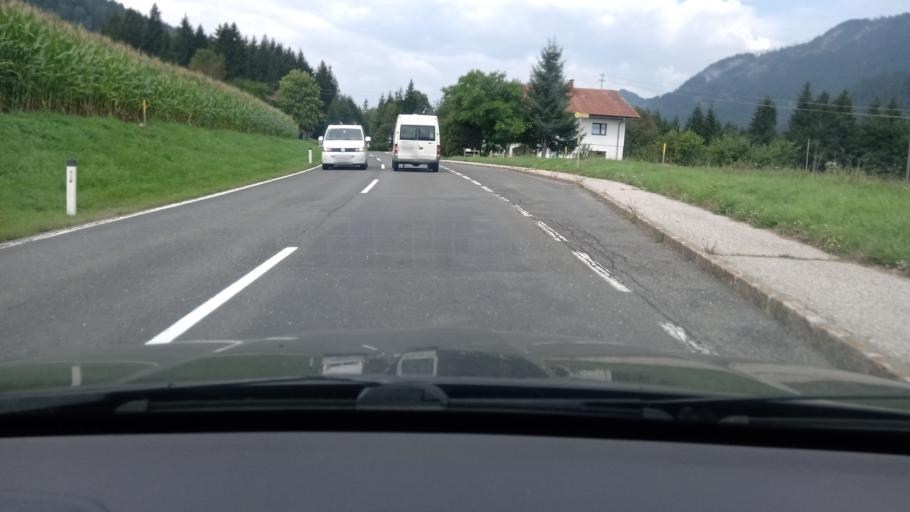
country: AT
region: Carinthia
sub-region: Politischer Bezirk Hermagor
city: Hermagor
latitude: 46.6452
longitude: 13.3367
